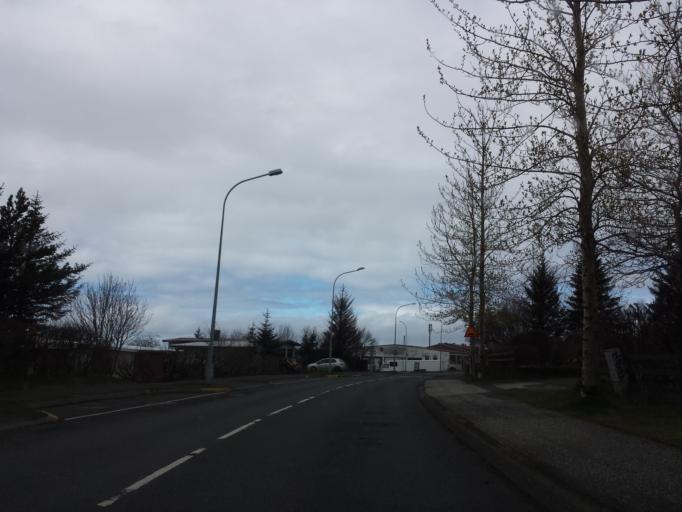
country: IS
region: Capital Region
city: Kopavogur
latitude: 64.1105
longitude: -21.9352
